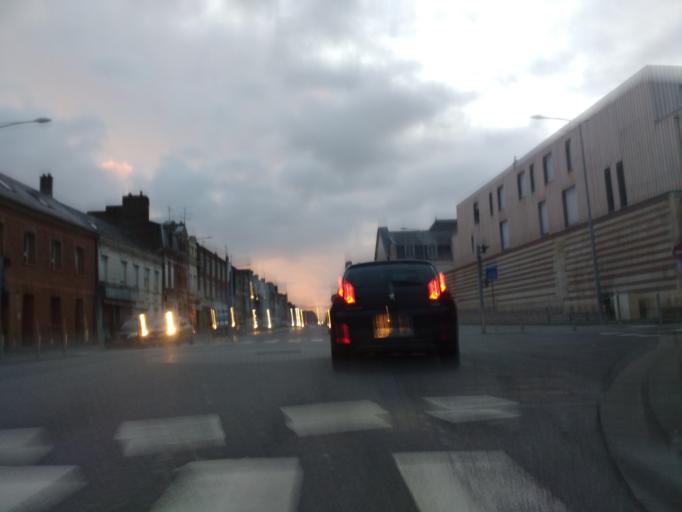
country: FR
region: Picardie
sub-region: Departement de la Somme
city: Amiens
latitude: 49.8889
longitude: 2.3110
